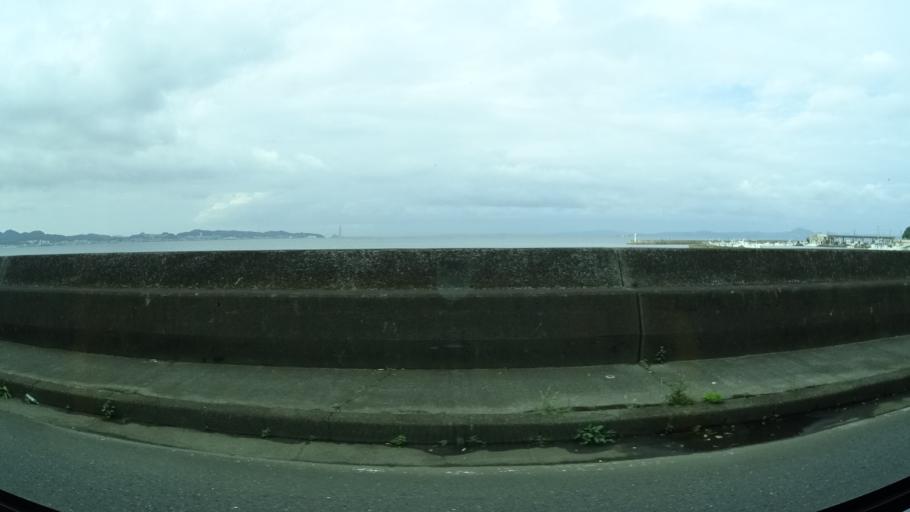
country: JP
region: Kanagawa
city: Miura
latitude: 35.1597
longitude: 139.6625
